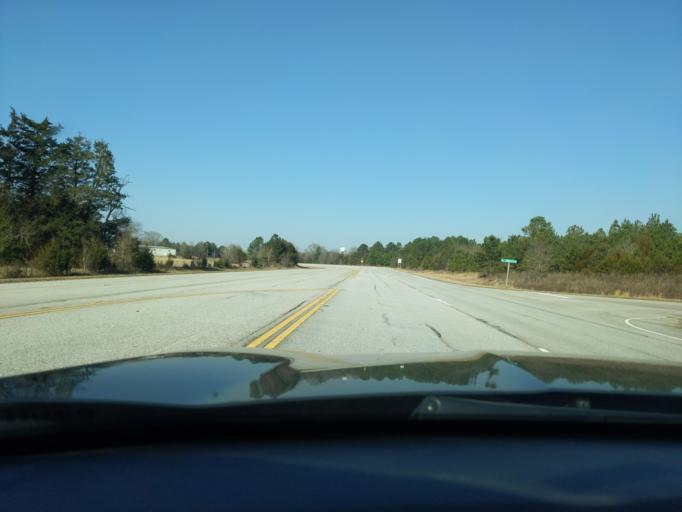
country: US
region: South Carolina
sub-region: Abbeville County
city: Calhoun Falls
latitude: 34.0963
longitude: -82.5759
